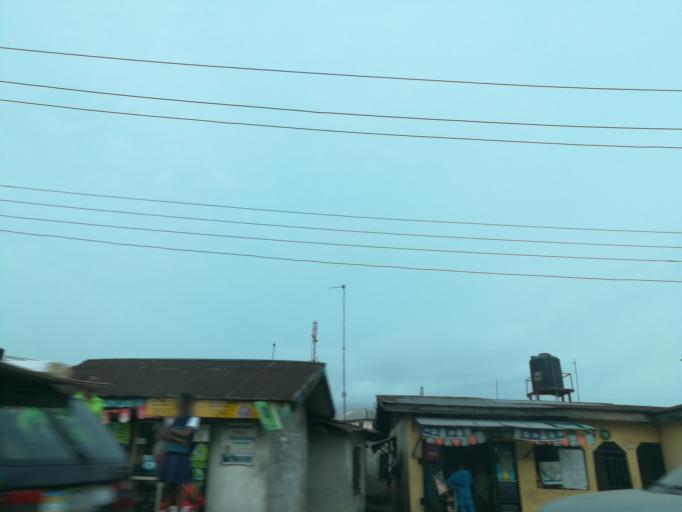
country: NG
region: Rivers
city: Port Harcourt
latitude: 4.8128
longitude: 7.0205
